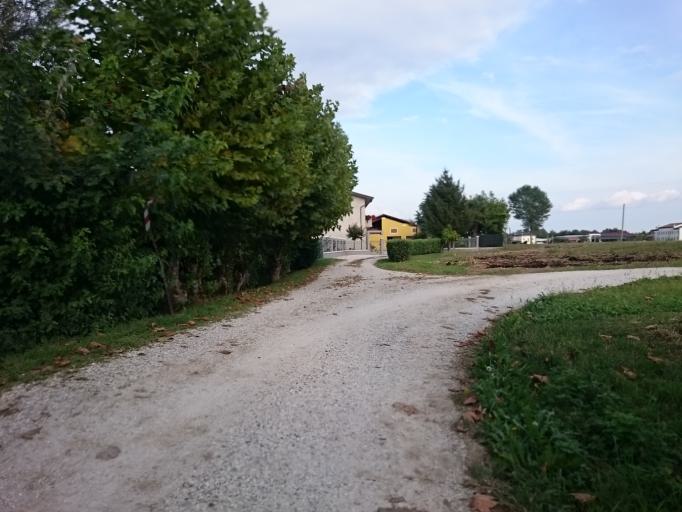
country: IT
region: Veneto
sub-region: Provincia di Vicenza
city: Grumolo delle Abbadesse
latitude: 45.5499
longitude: 11.6799
